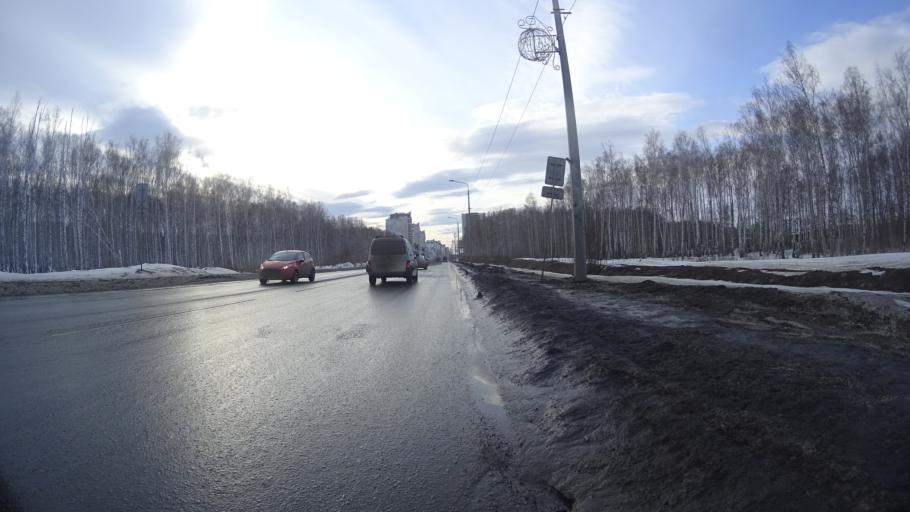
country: RU
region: Chelyabinsk
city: Roshchino
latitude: 55.2085
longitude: 61.3137
